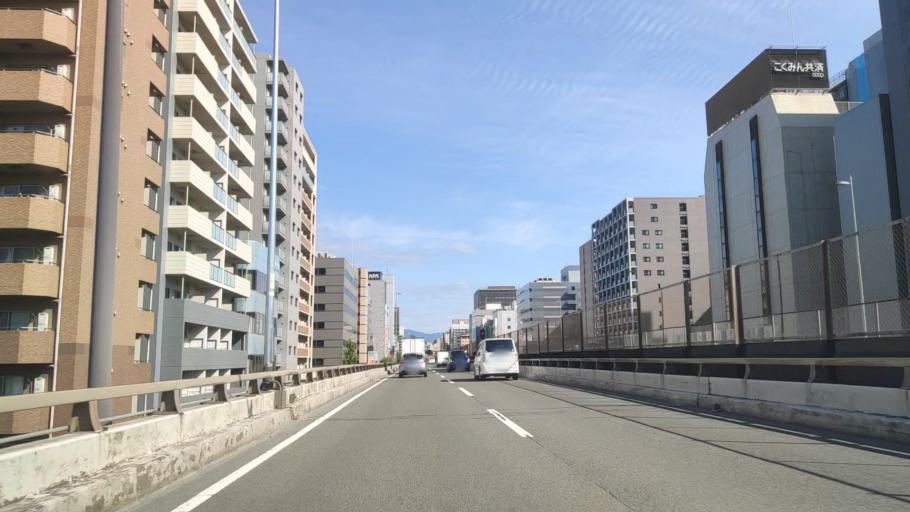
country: JP
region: Osaka
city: Suita
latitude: 34.7543
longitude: 135.4967
